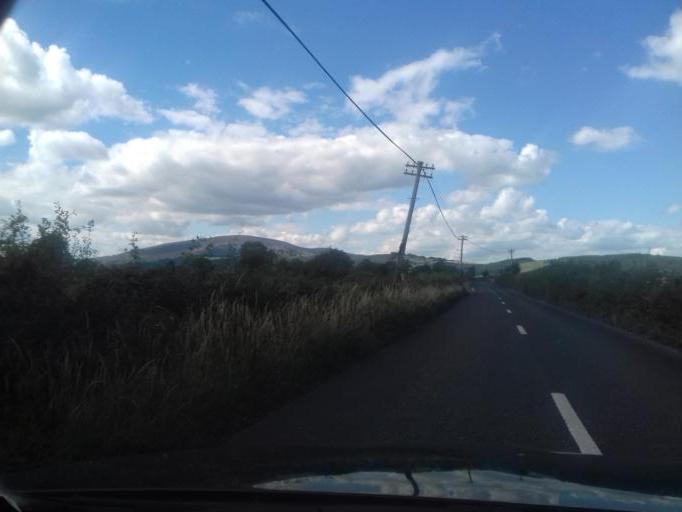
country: IE
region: Munster
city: Carrick-on-Suir
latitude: 52.3778
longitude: -7.4539
